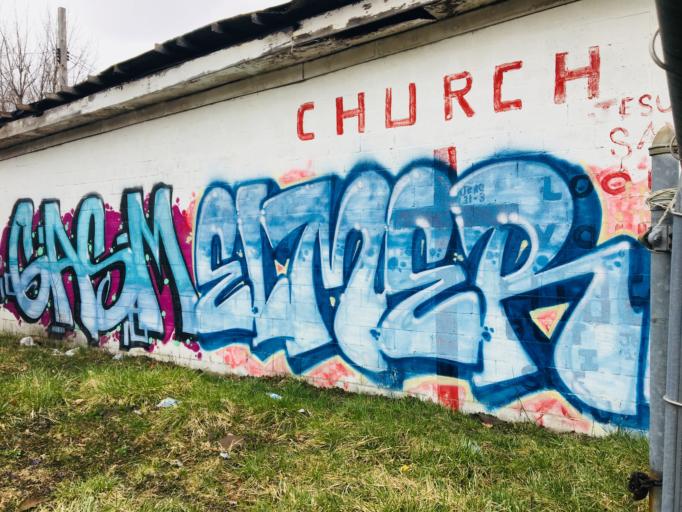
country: US
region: Michigan
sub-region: Macomb County
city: Eastpointe
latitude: 42.4203
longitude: -82.9855
